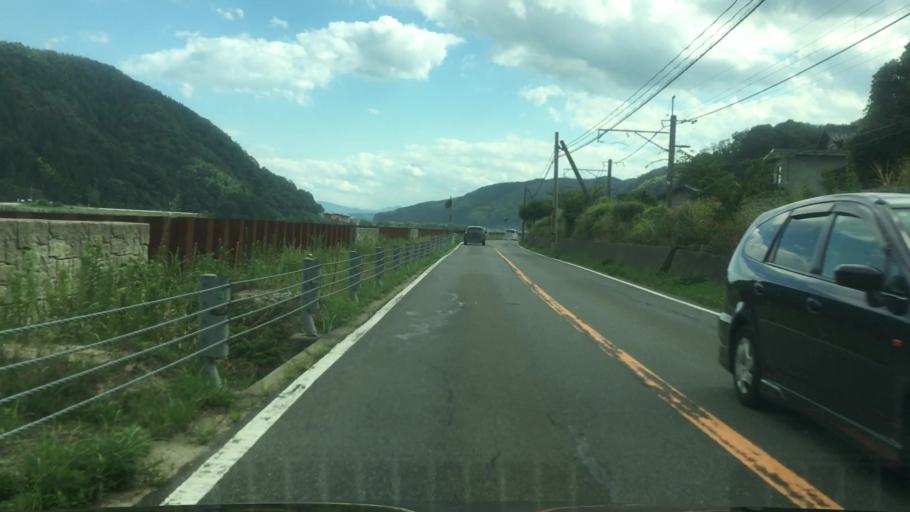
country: JP
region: Hyogo
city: Toyooka
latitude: 35.5987
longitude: 134.8019
